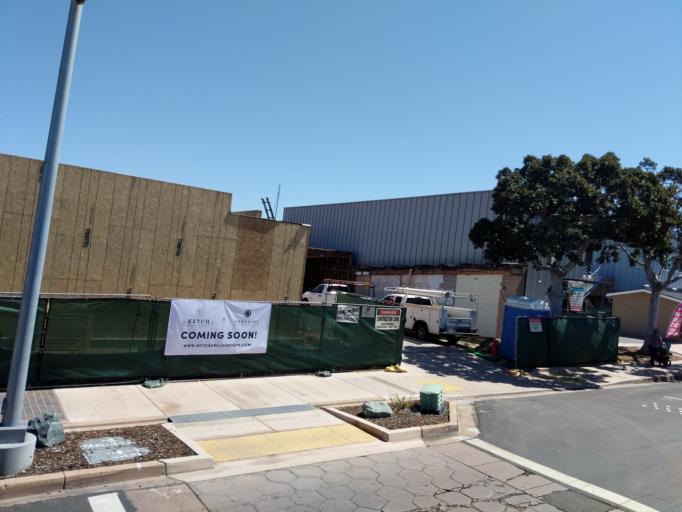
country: US
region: California
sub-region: San Diego County
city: Coronado
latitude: 32.7206
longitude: -117.2276
